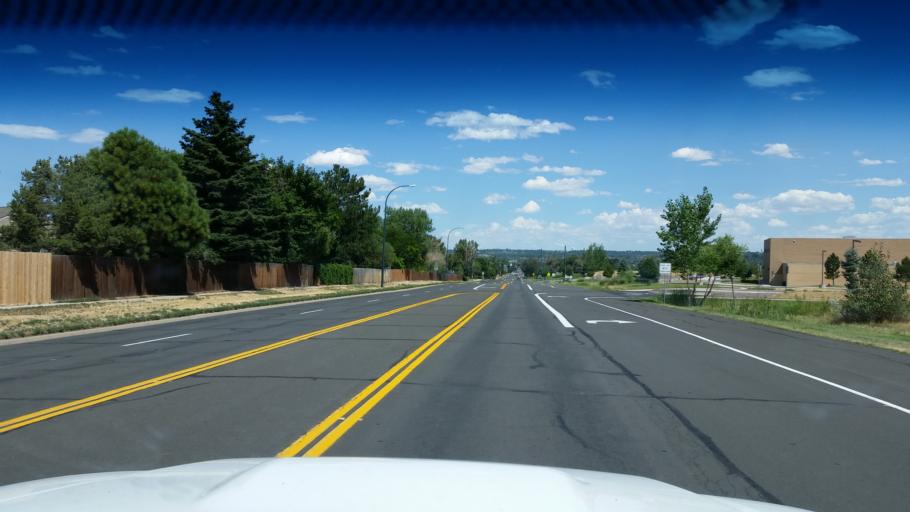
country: US
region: Colorado
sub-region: Broomfield County
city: Broomfield
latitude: 39.8782
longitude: -105.1146
